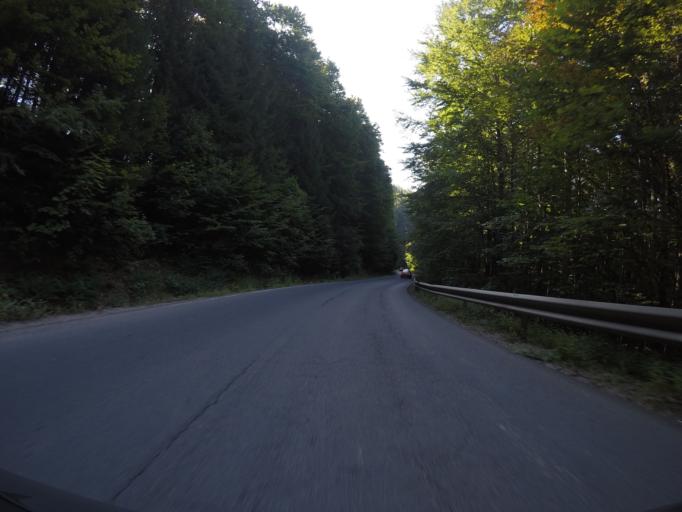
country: RO
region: Brasov
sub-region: Comuna Cristian
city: Cristian
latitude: 45.5857
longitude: 25.5143
